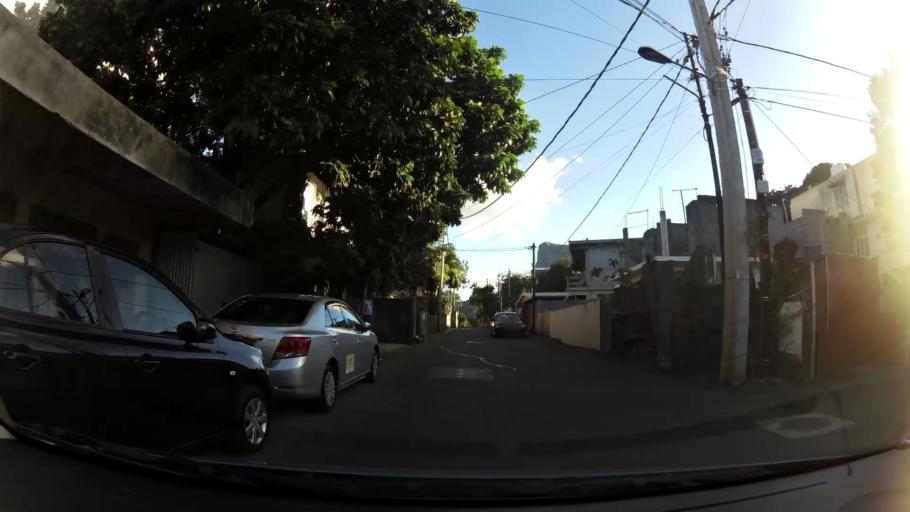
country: MU
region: Plaines Wilhems
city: Quatre Bornes
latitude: -20.2543
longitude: 57.4708
